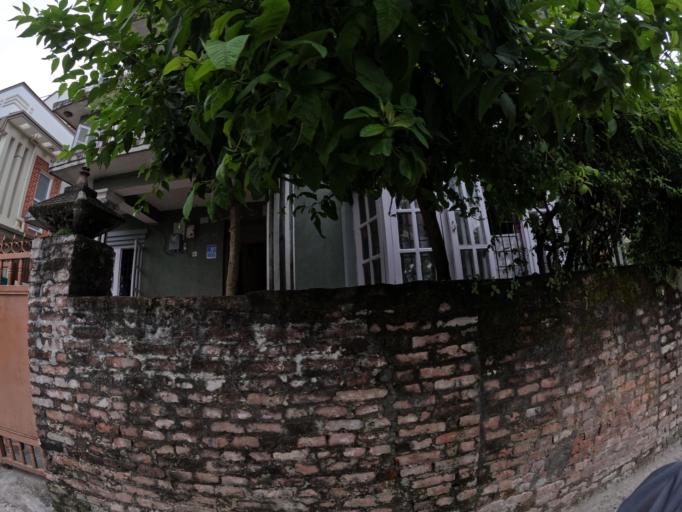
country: NP
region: Central Region
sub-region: Bagmati Zone
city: Kathmandu
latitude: 27.7423
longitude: 85.3186
